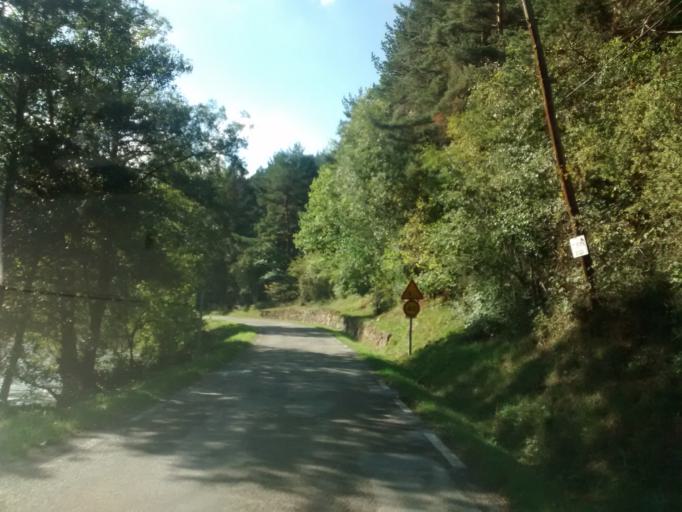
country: ES
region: Cantabria
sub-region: Provincia de Cantabria
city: Reinosa
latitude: 42.9389
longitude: -4.0494
